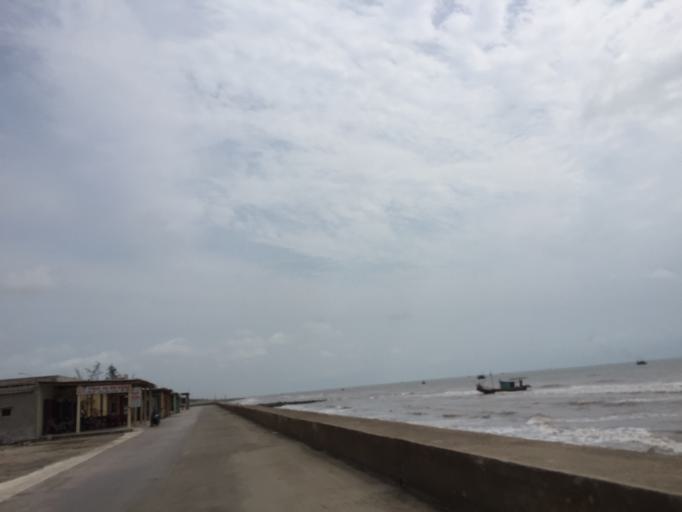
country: VN
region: Ninh Binh
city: Thi Tran Phat Diem
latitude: 20.0328
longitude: 106.2261
